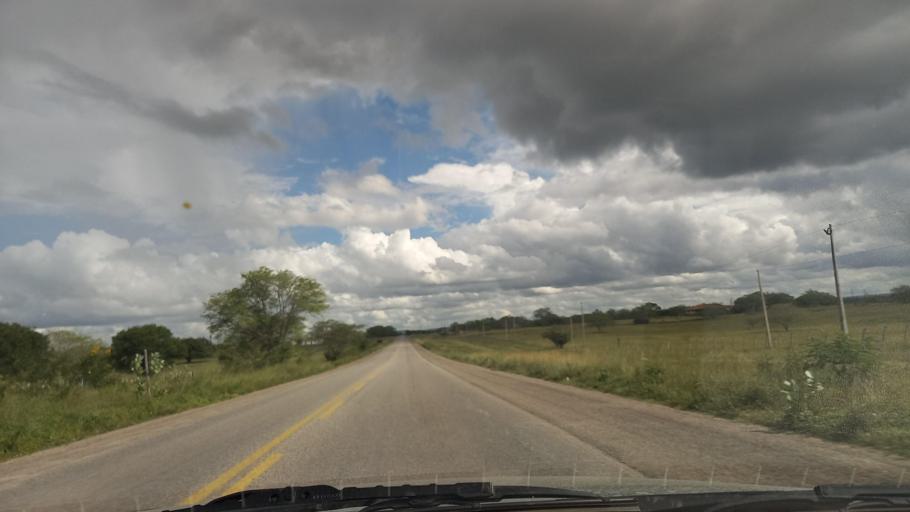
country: BR
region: Pernambuco
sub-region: Cachoeirinha
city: Cachoeirinha
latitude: -8.5247
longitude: -36.2599
